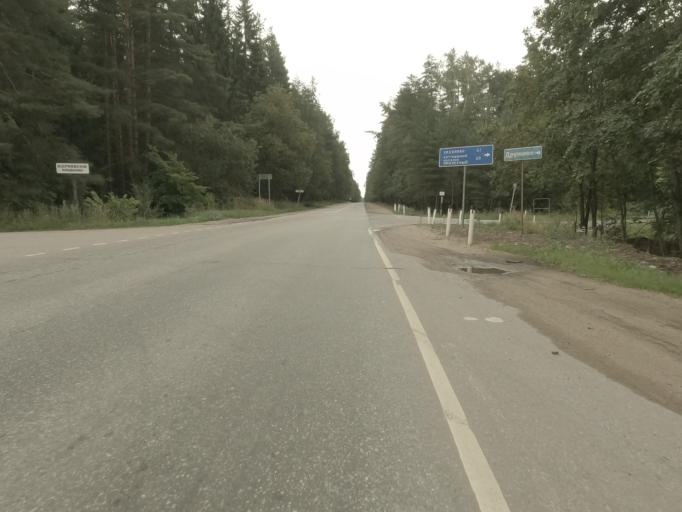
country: RU
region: Leningrad
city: Koltushi
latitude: 59.8933
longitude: 30.7442
